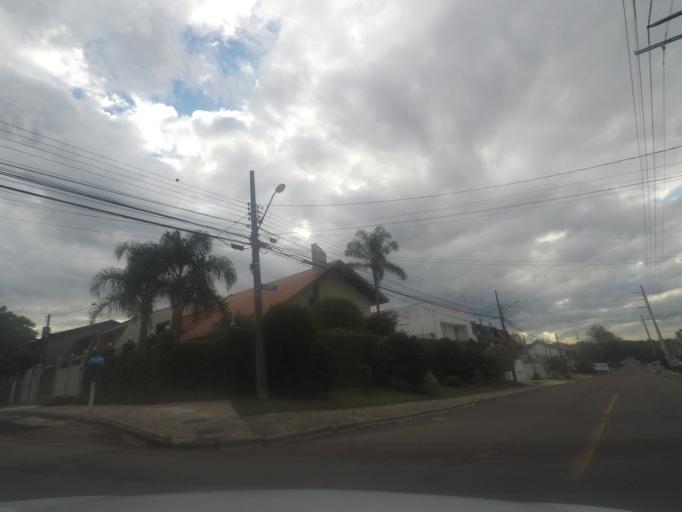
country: BR
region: Parana
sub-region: Pinhais
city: Pinhais
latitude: -25.4617
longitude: -49.2214
